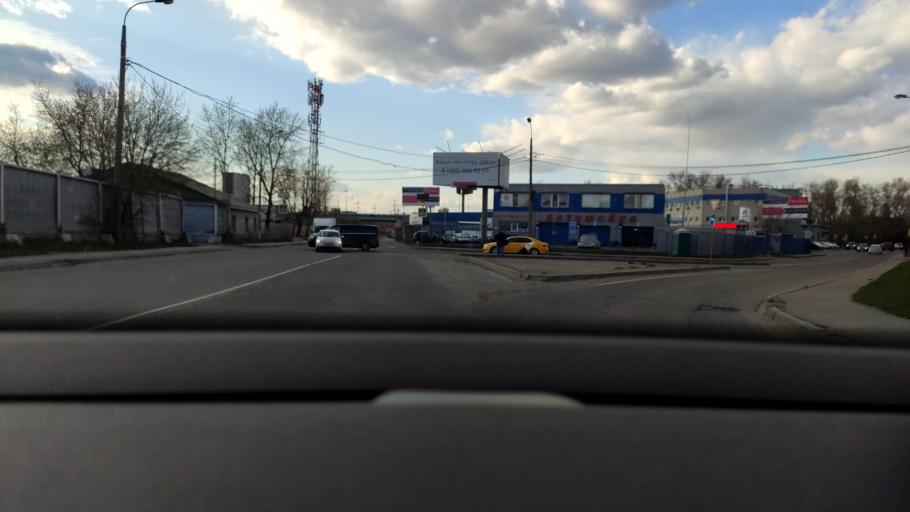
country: RU
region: Moskovskaya
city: Reutov
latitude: 55.7784
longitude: 37.8650
